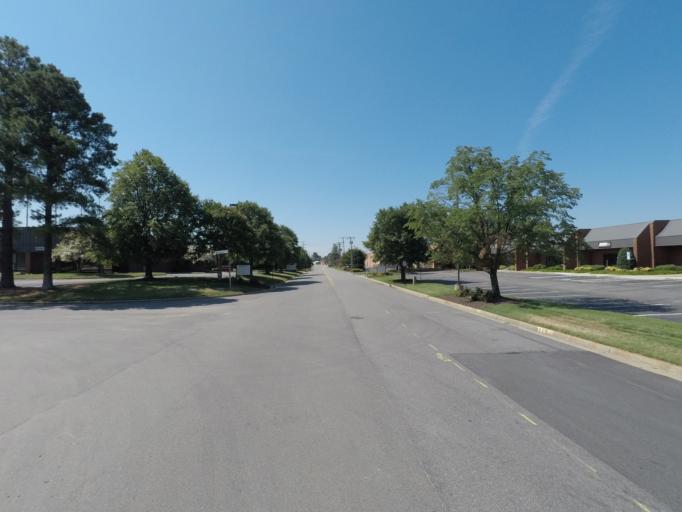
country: US
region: Virginia
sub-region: Henrico County
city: Dumbarton
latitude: 37.5807
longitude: -77.4796
